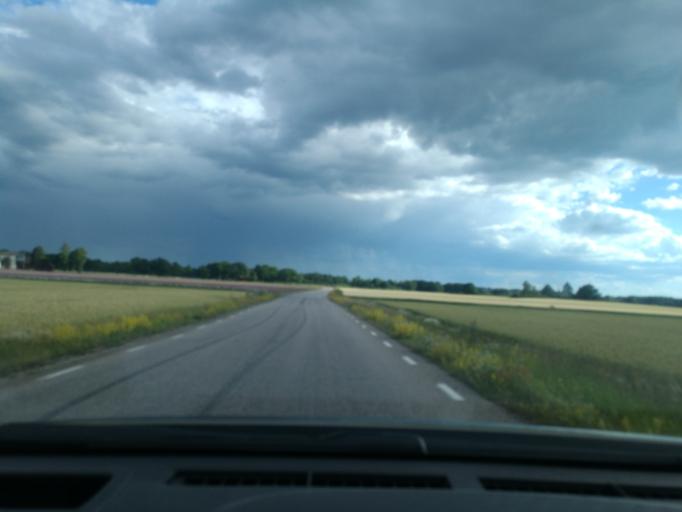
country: SE
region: Soedermanland
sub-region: Eskilstuna Kommun
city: Arla
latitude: 59.4284
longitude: 16.7097
